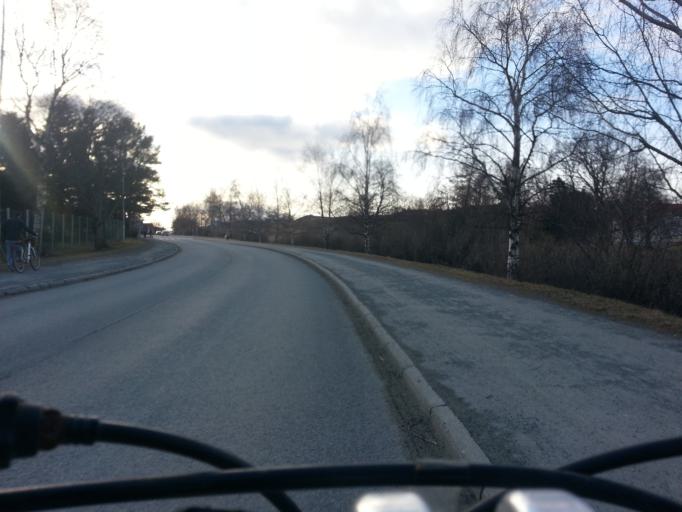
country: NO
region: Sor-Trondelag
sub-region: Trondheim
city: Trondheim
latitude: 63.4500
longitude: 10.4531
